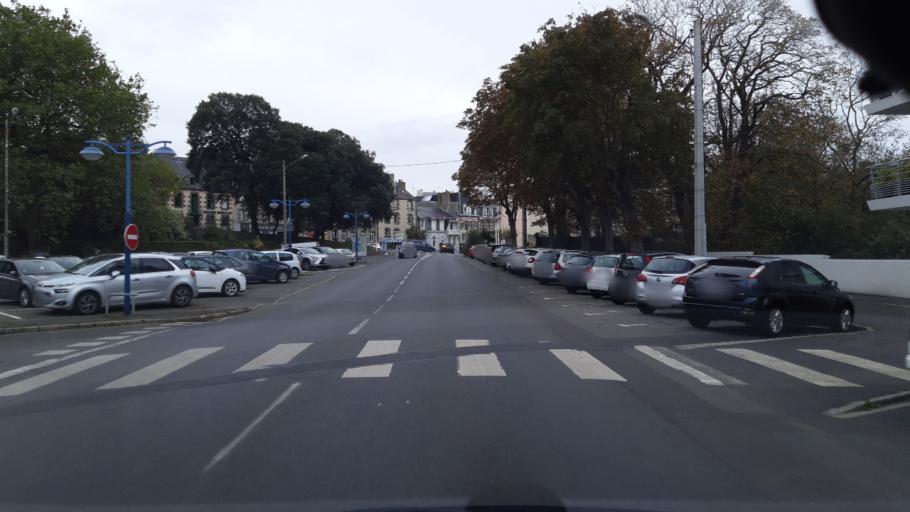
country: FR
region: Lower Normandy
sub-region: Departement de la Manche
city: Donville-les-Bains
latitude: 48.8387
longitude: -1.5879
